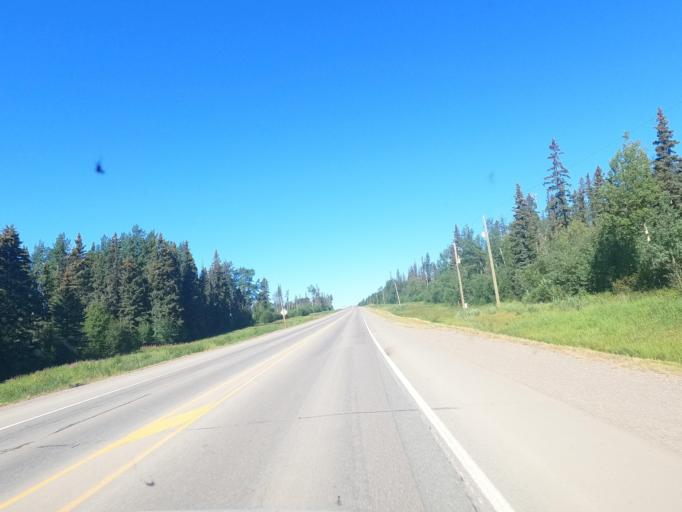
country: CA
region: British Columbia
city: Fort St. John
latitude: 56.7137
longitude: -121.7598
